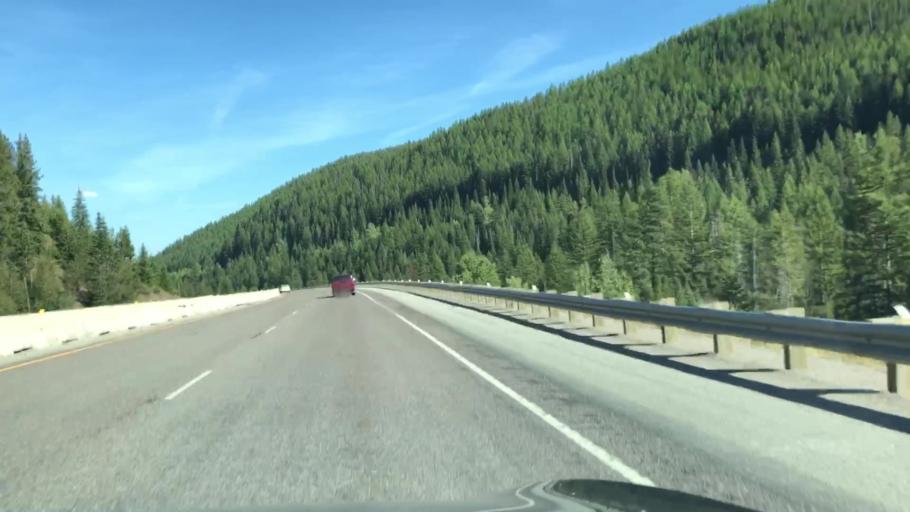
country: US
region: Montana
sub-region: Sanders County
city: Thompson Falls
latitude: 47.4160
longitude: -115.5781
